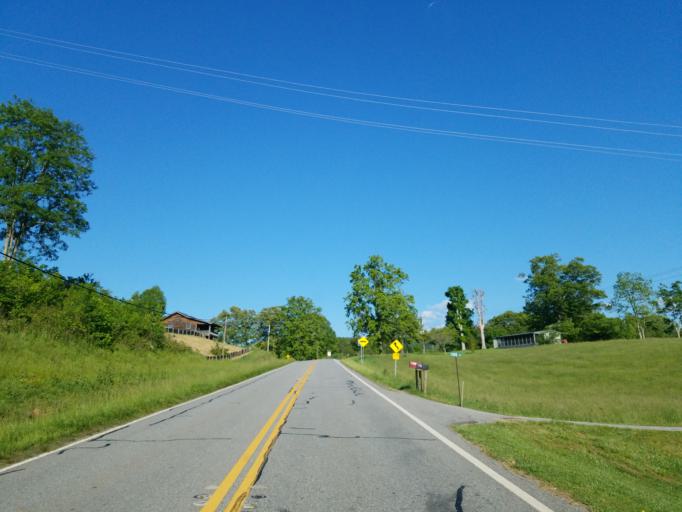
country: US
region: Georgia
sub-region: Fannin County
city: Blue Ridge
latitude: 34.8450
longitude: -84.1982
